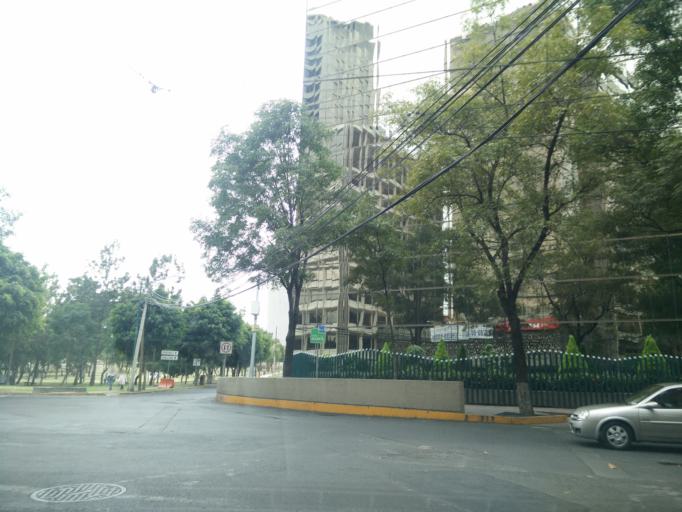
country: MX
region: Mexico City
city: Miguel Hidalgo
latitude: 19.4298
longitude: -99.2027
